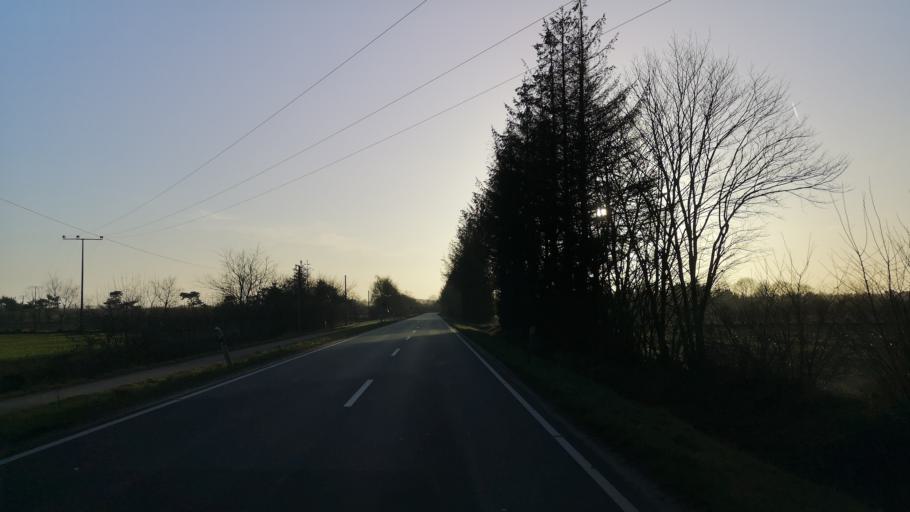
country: DE
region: Schleswig-Holstein
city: Sieverstedt
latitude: 54.6726
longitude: 9.4812
